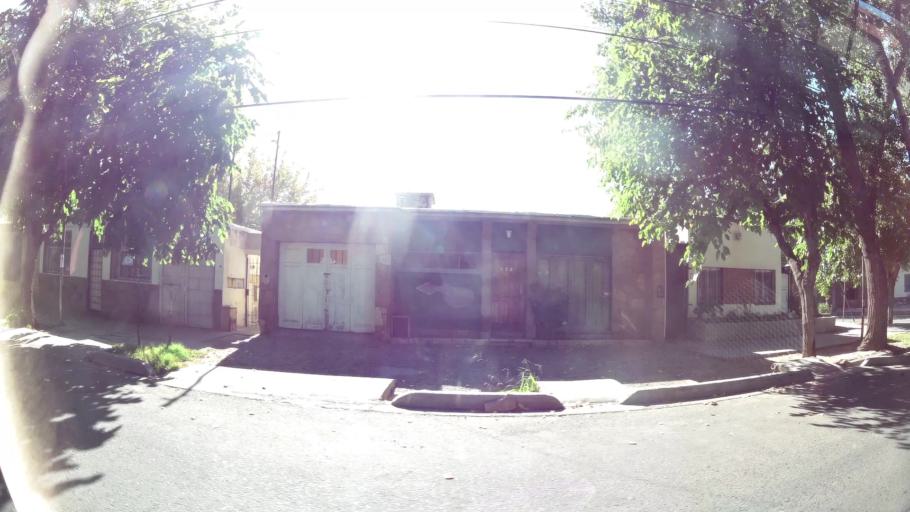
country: AR
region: Mendoza
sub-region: Departamento de Godoy Cruz
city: Godoy Cruz
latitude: -32.9356
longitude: -68.8586
